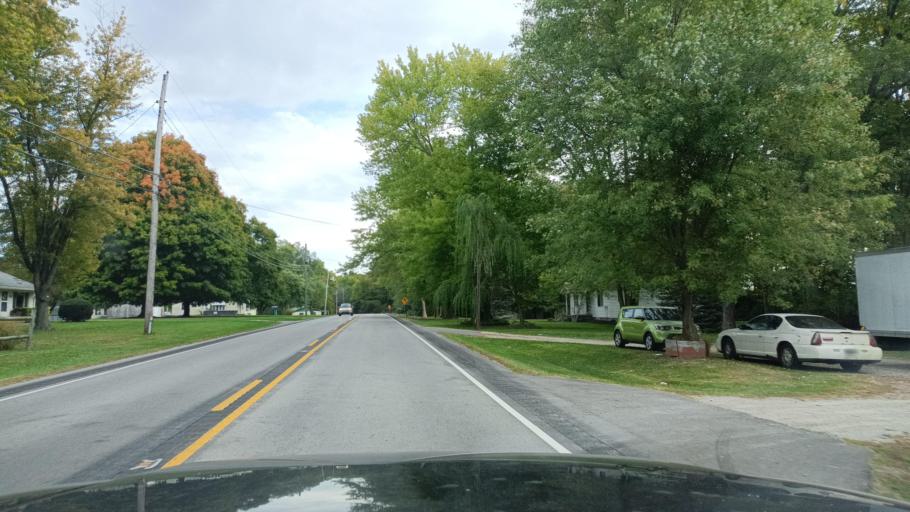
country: US
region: Indiana
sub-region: Delaware County
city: Daleville
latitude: 40.1500
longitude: -85.5370
